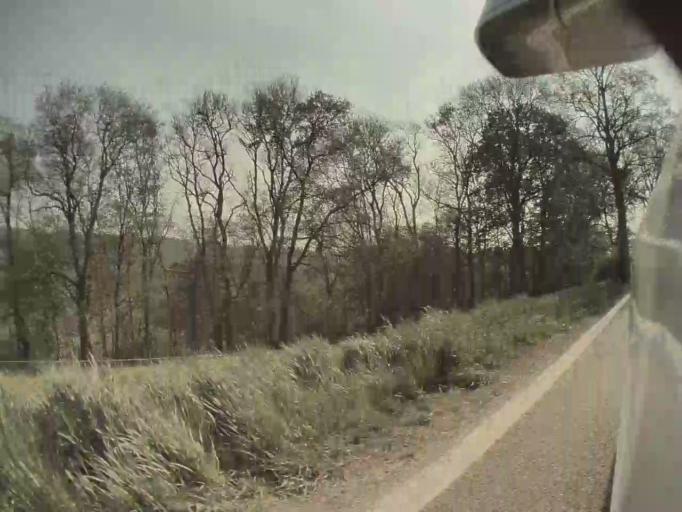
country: BE
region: Wallonia
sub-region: Province de Namur
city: Havelange
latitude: 50.3306
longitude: 5.2725
